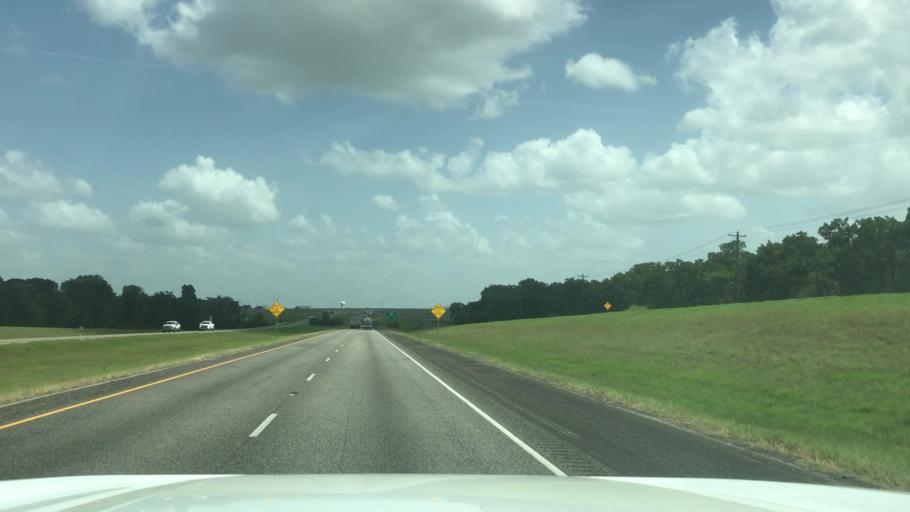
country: US
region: Texas
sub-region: Brazos County
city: Bryan
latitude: 30.7345
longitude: -96.4352
